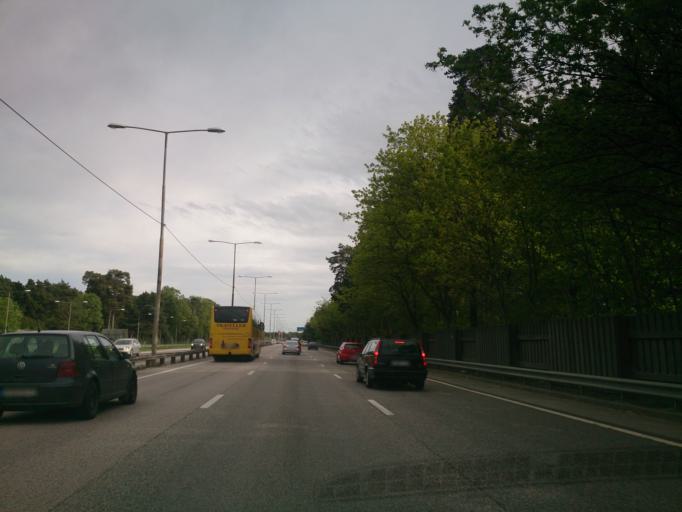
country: SE
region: Stockholm
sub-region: Stockholms Kommun
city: Arsta
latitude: 59.2696
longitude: 18.0952
